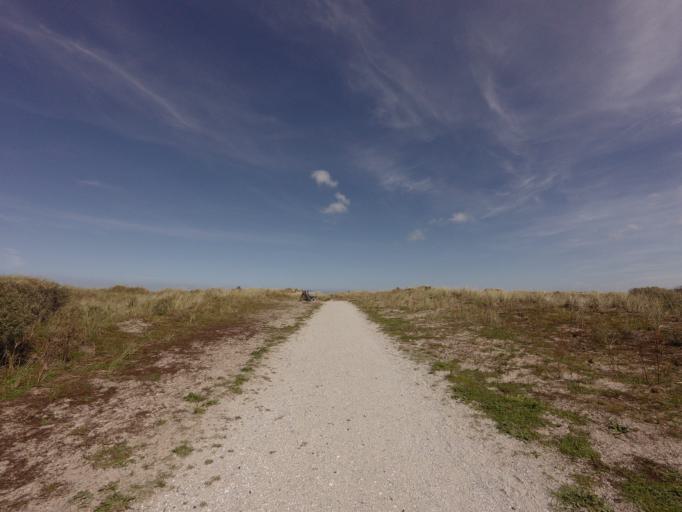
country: NL
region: Friesland
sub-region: Gemeente Ameland
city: Hollum
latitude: 53.4583
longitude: 5.6990
